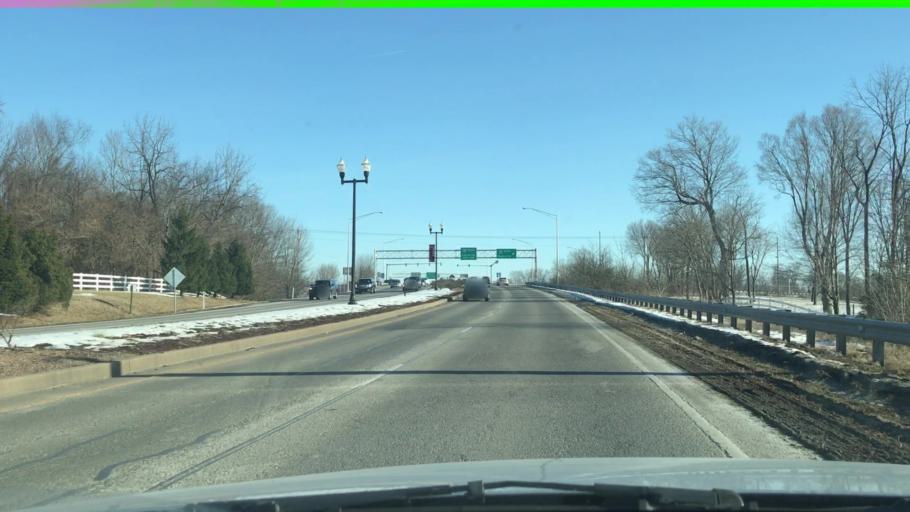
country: US
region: Kentucky
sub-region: Warren County
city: Bowling Green
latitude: 36.9797
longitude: -86.3944
